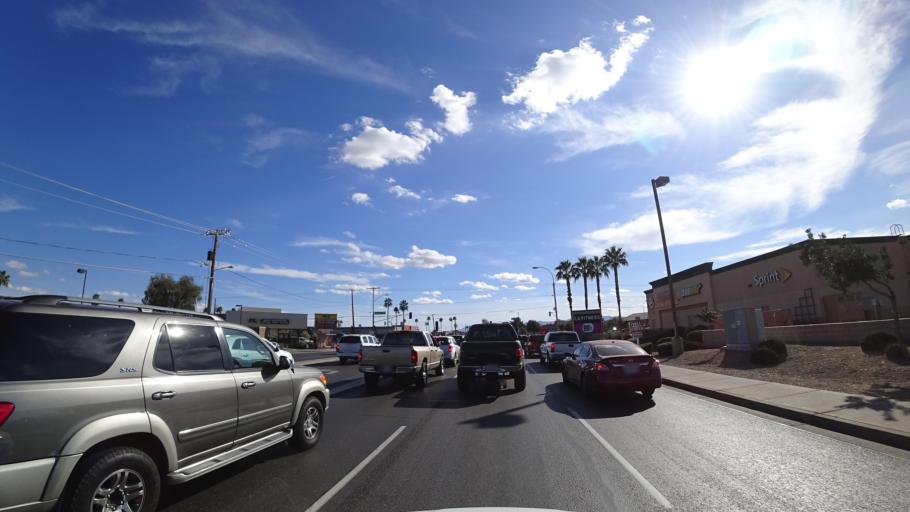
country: US
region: Arizona
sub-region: Maricopa County
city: Tolleson
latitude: 33.4811
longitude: -112.2207
